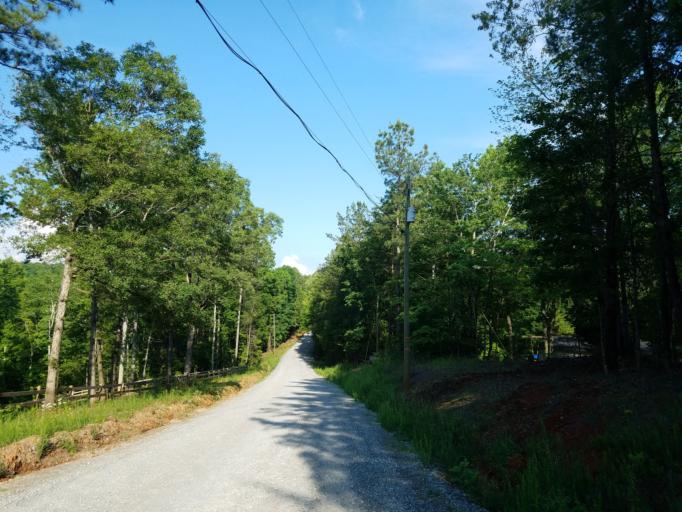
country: US
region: Georgia
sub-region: Pickens County
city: Nelson
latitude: 34.3719
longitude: -84.3398
